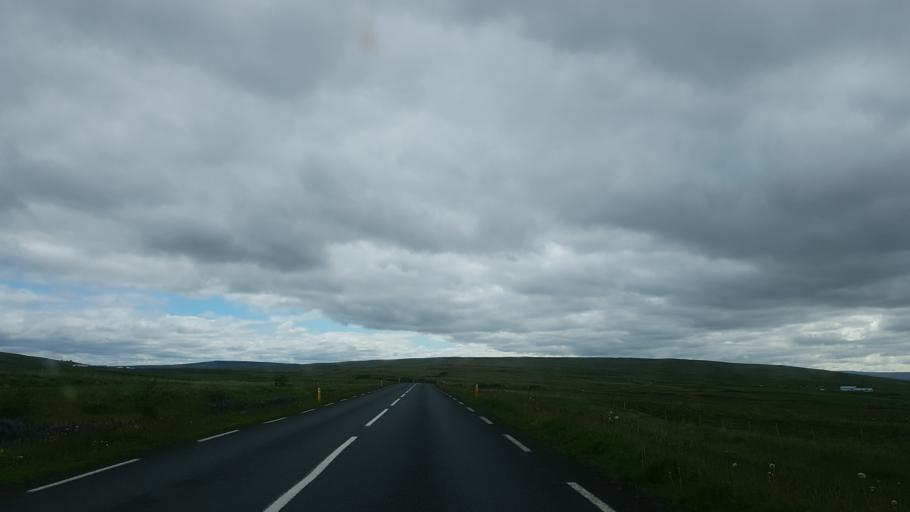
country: IS
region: Northwest
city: Saudarkrokur
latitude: 65.3637
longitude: -20.8972
